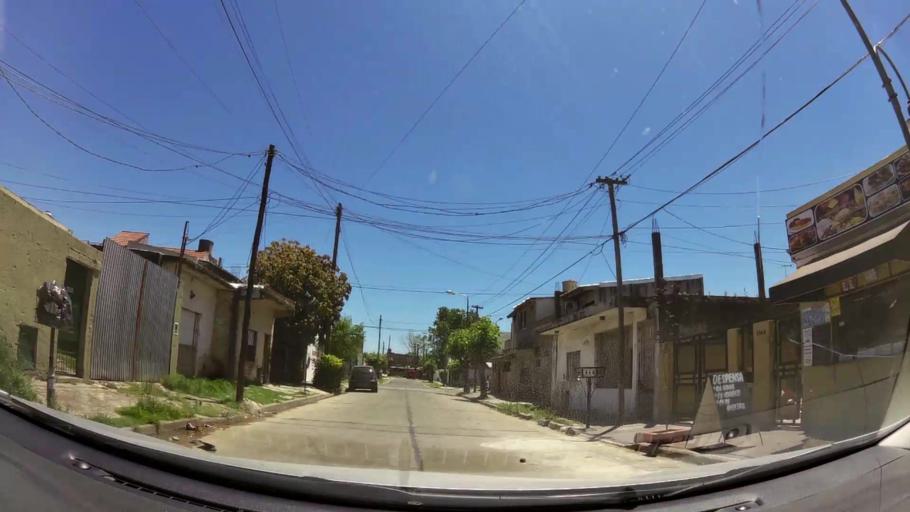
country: AR
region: Buenos Aires
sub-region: Partido de Tigre
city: Tigre
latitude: -34.4520
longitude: -58.5577
